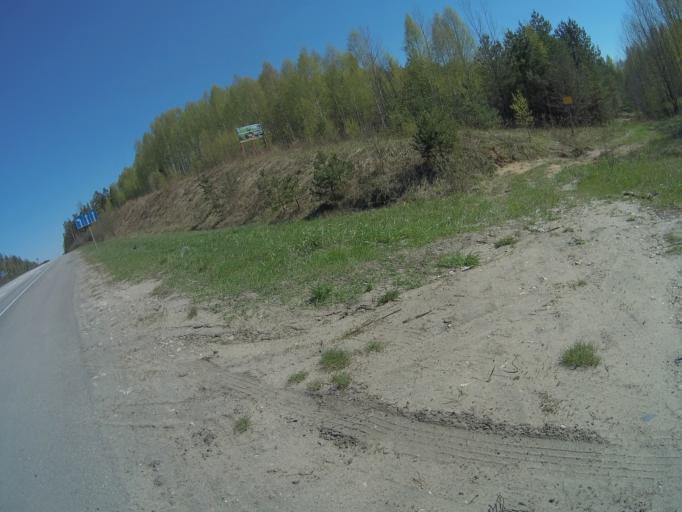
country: RU
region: Vladimir
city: Orgtrud
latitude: 56.1034
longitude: 40.6629
